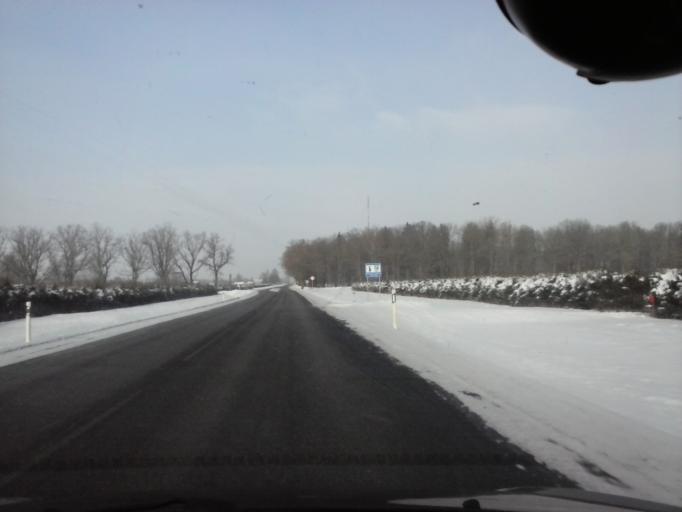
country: EE
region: Viljandimaa
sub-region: Abja vald
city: Abja-Paluoja
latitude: 58.3146
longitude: 25.3018
